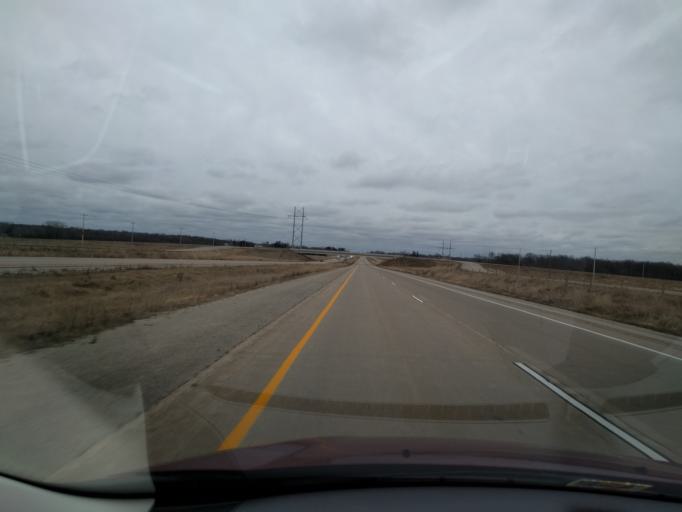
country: US
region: Wisconsin
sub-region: Winnebago County
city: Winneconne
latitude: 44.1728
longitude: -88.6645
